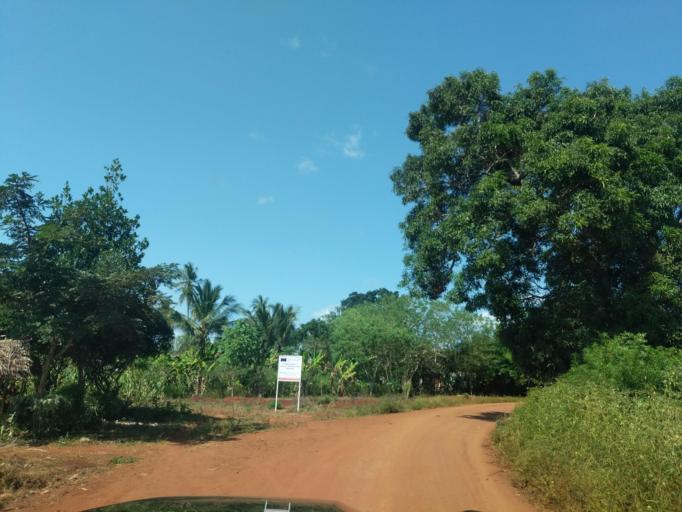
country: TZ
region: Tanga
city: Muheza
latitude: -5.3815
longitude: 38.5814
